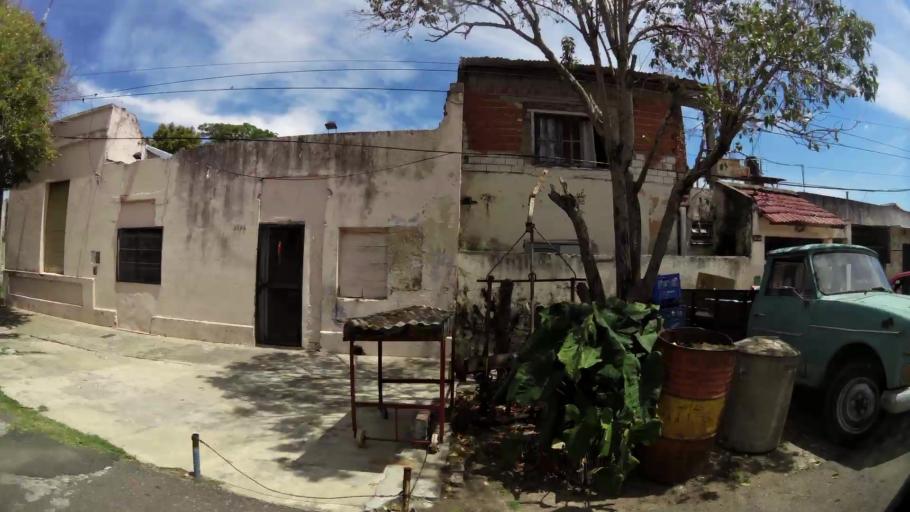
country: AR
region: Santa Fe
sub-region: Departamento de Rosario
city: Rosario
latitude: -32.9838
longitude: -60.6322
